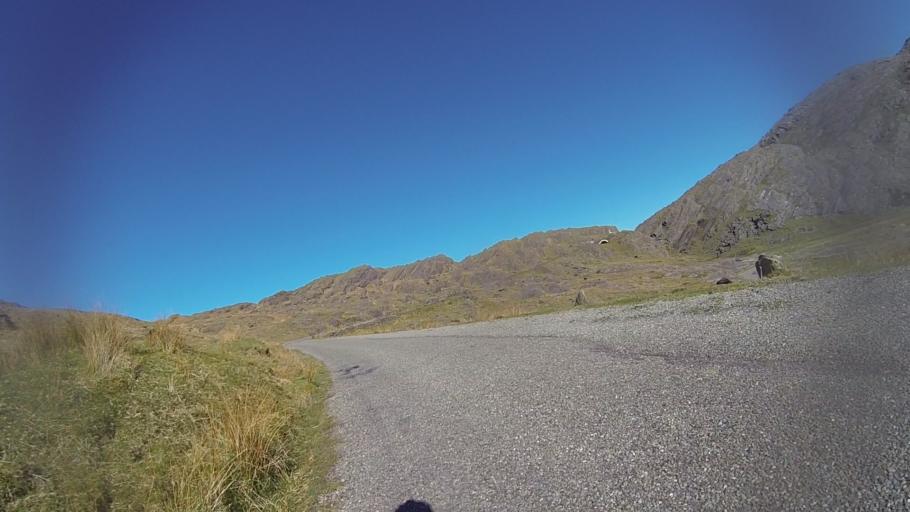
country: IE
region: Munster
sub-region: Ciarrai
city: Kenmare
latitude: 51.7175
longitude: -9.7529
